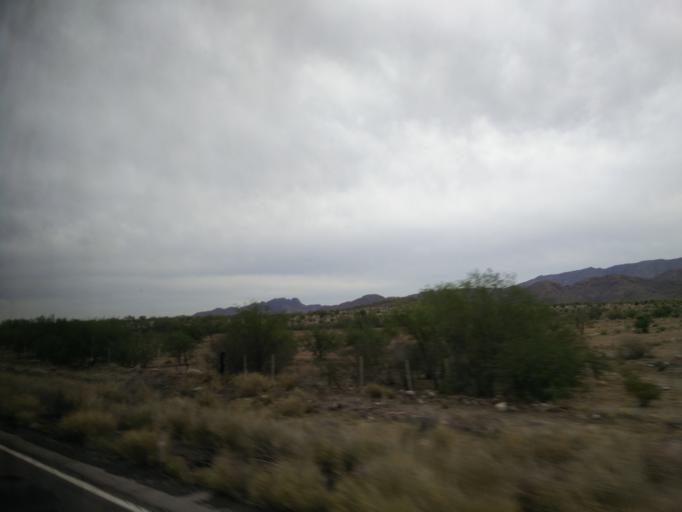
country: MX
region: Sonora
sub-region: Hermosillo
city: Miguel Aleman (La Doce)
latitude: 28.5249
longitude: -111.0469
